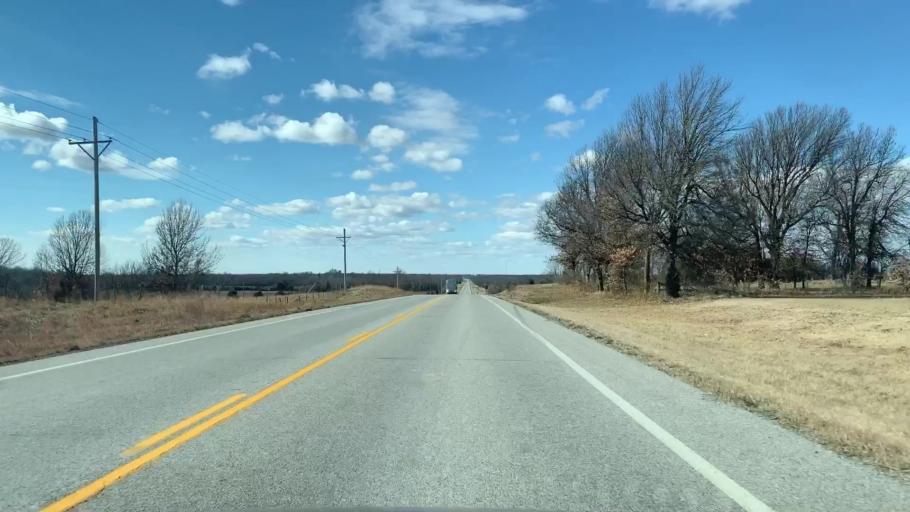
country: US
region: Kansas
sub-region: Cherokee County
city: Columbus
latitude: 37.1781
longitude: -94.7875
